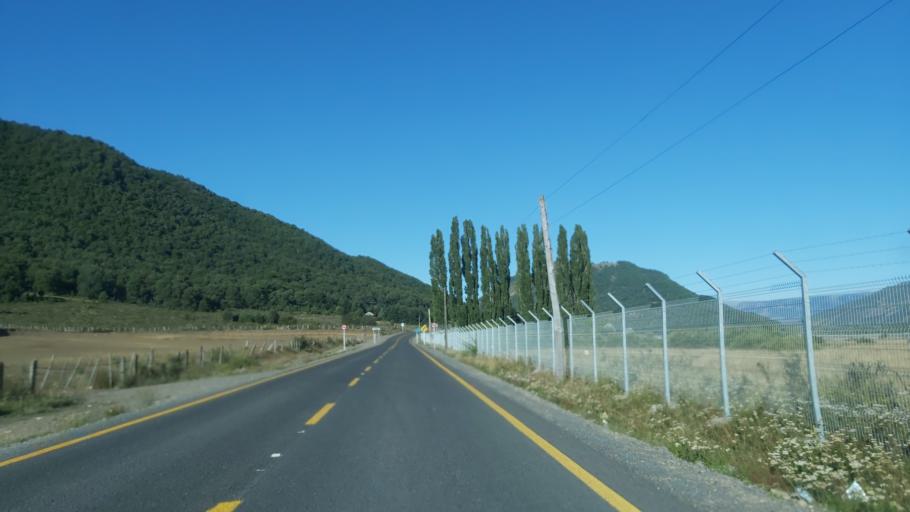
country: AR
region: Neuquen
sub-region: Departamento de Loncopue
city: Loncopue
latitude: -38.4475
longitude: -71.3613
